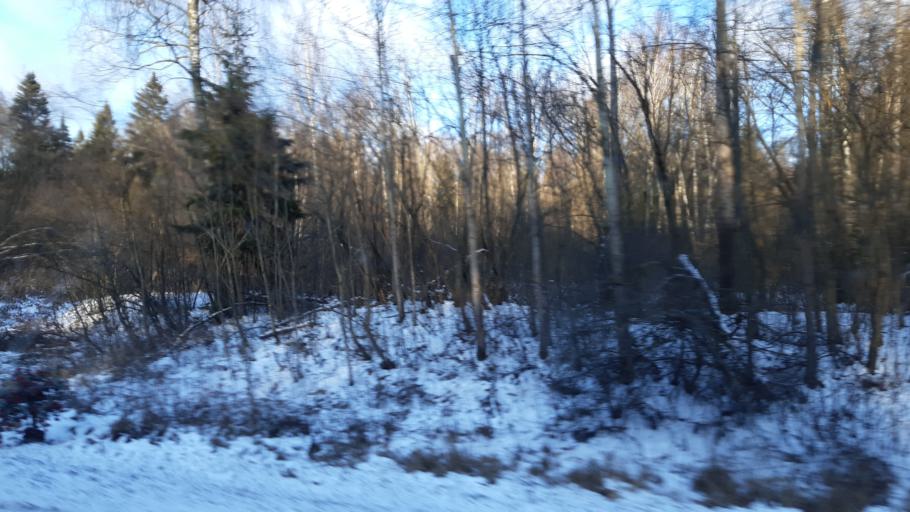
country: RU
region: Vladimir
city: Arsaki
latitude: 56.2955
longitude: 38.3669
